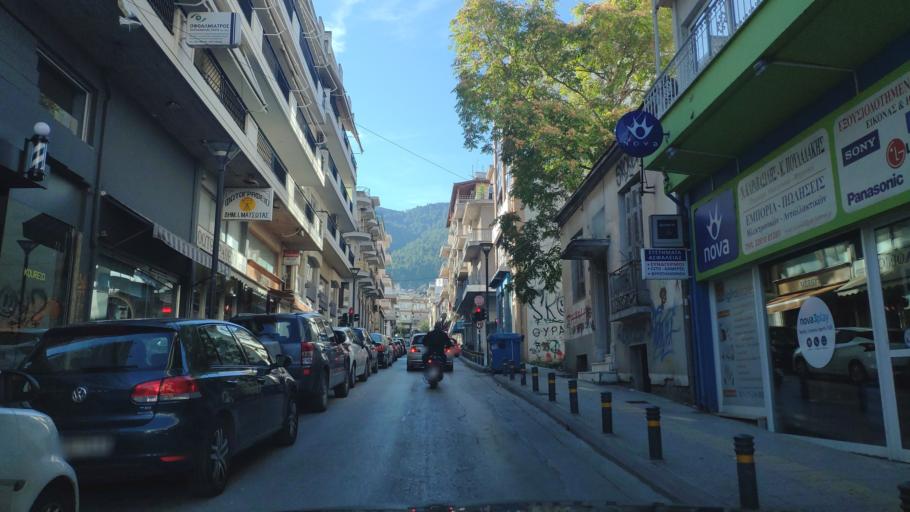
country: GR
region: Central Greece
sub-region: Nomos Voiotias
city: Livadeia
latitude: 38.4389
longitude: 22.8777
